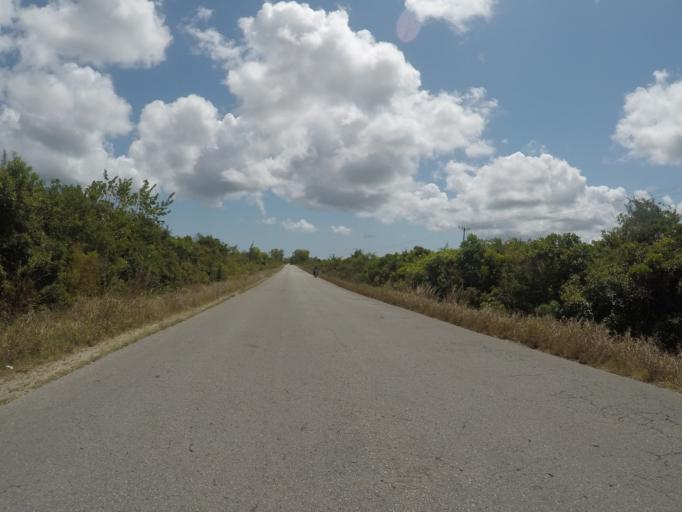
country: TZ
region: Zanzibar Central/South
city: Nganane
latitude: -6.2848
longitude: 39.4578
